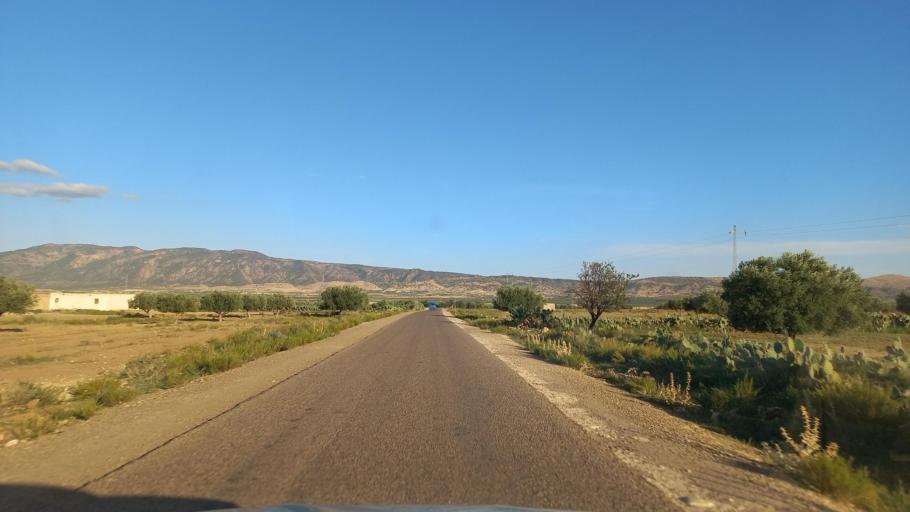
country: TN
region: Al Qasrayn
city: Sbiba
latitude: 35.4125
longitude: 9.1286
